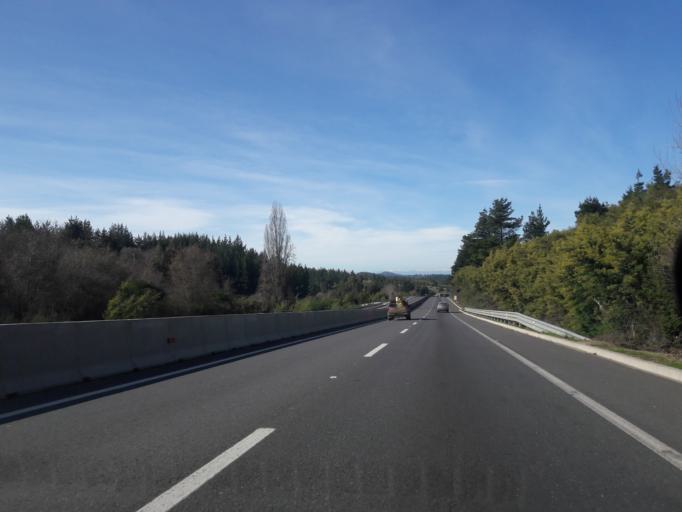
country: CL
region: Biobio
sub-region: Provincia de Biobio
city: Yumbel
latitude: -36.9643
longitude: -72.7036
